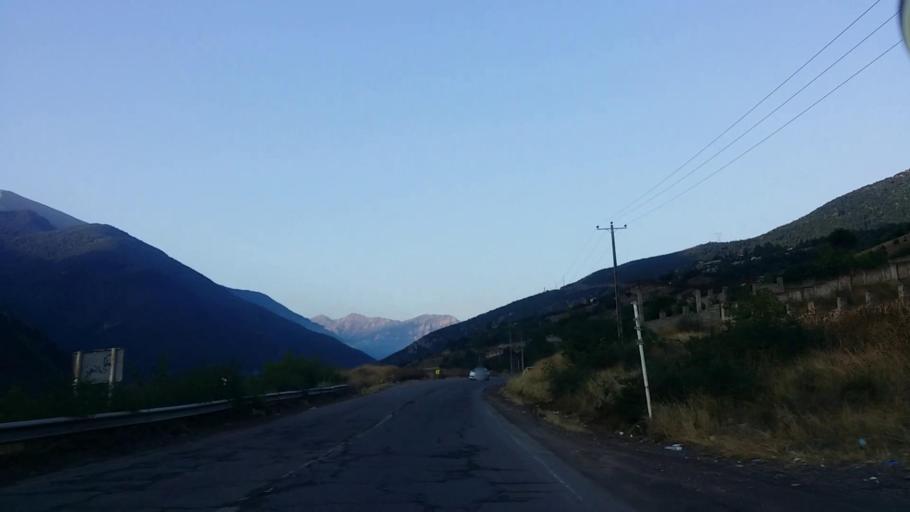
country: IR
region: Mazandaran
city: Chalus
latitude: 36.4072
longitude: 51.2798
